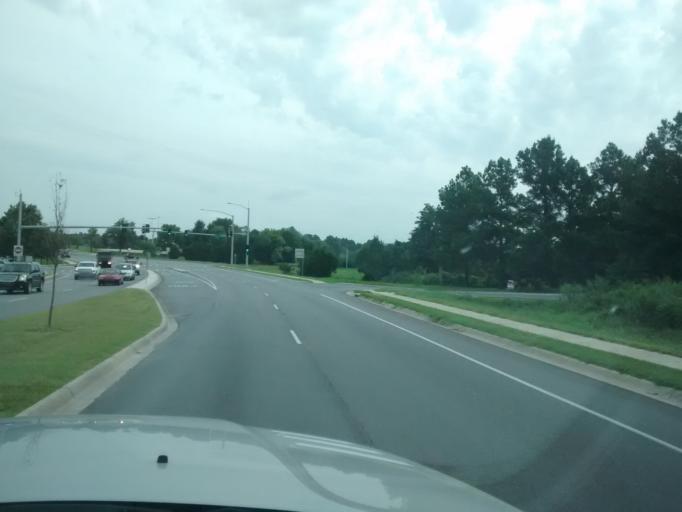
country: US
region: Arkansas
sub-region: Washington County
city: Johnson
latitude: 36.1282
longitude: -94.1185
